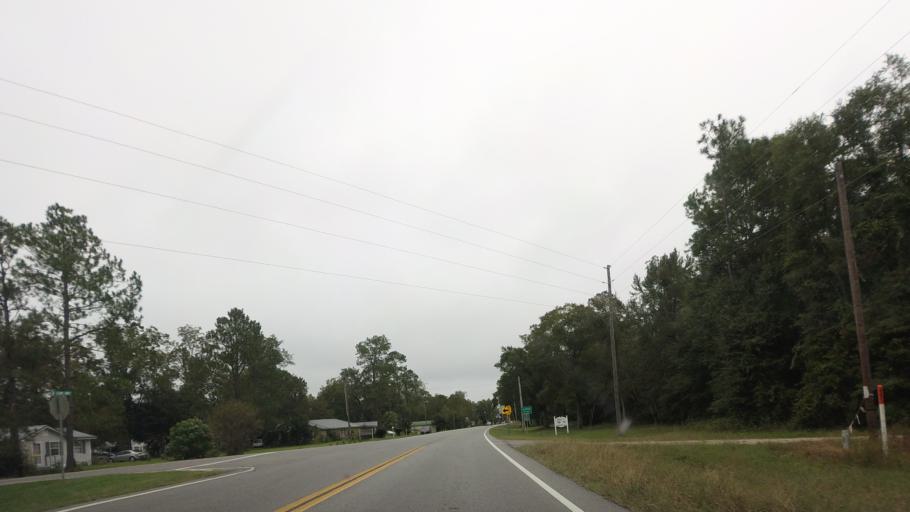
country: US
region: Georgia
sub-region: Berrien County
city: Enigma
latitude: 31.3742
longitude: -83.2261
